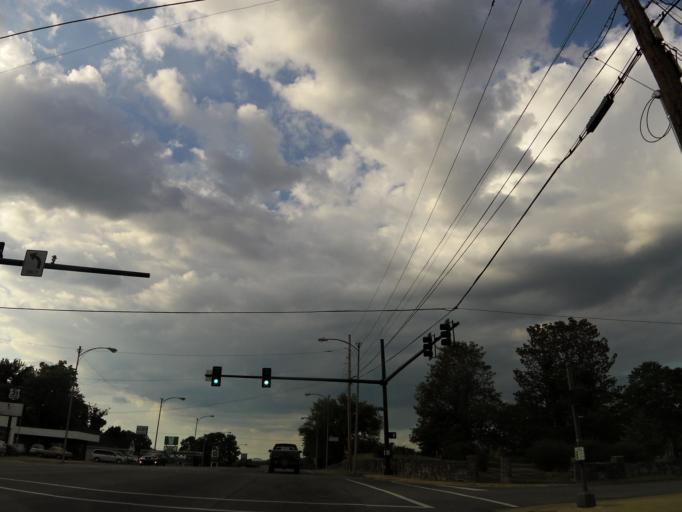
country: US
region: Tennessee
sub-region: Maury County
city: Columbia
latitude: 35.6188
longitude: -87.0349
